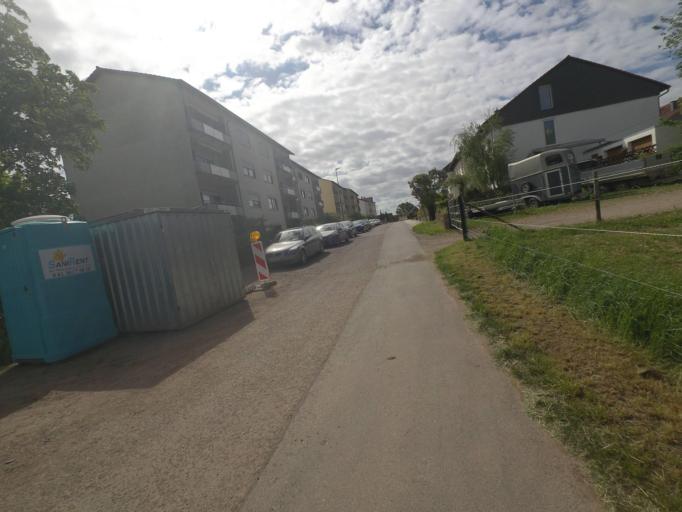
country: DE
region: Rheinland-Pfalz
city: Kirchheimbolanden
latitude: 49.6723
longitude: 8.0036
